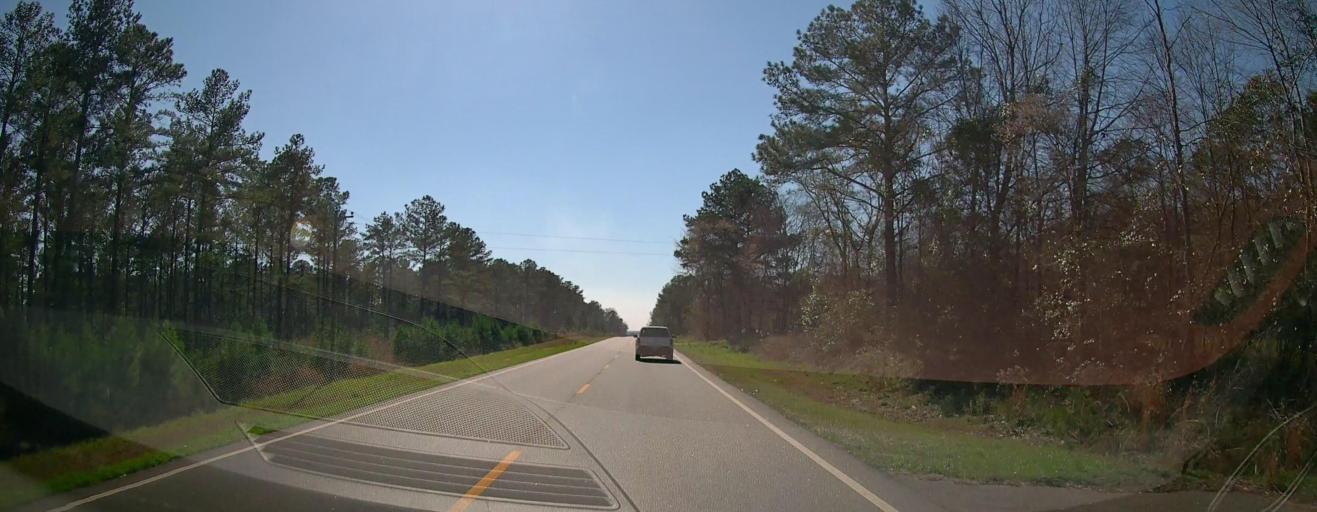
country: US
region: Georgia
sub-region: Dooly County
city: Unadilla
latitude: 32.3355
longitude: -83.8572
